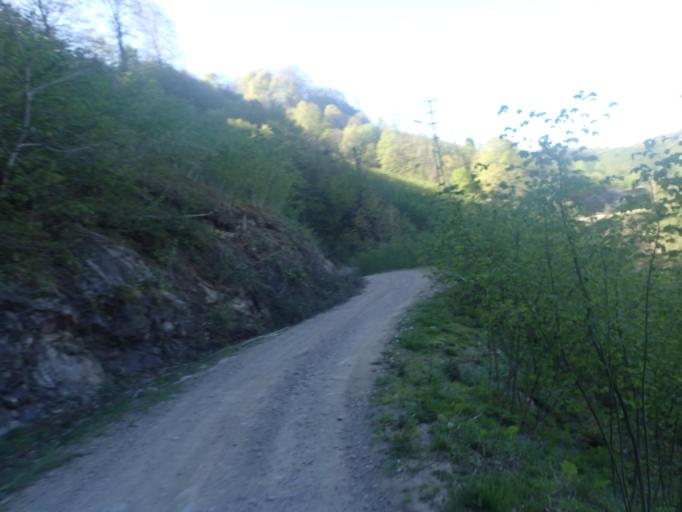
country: TR
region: Ordu
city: Kabaduz
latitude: 40.8178
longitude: 37.9056
